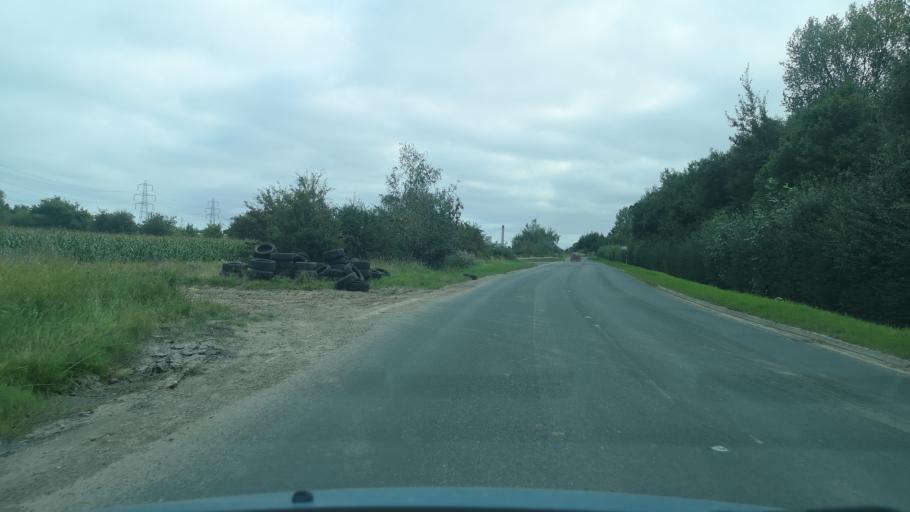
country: GB
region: England
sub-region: City and Borough of Wakefield
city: Knottingley
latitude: 53.6923
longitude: -1.1999
